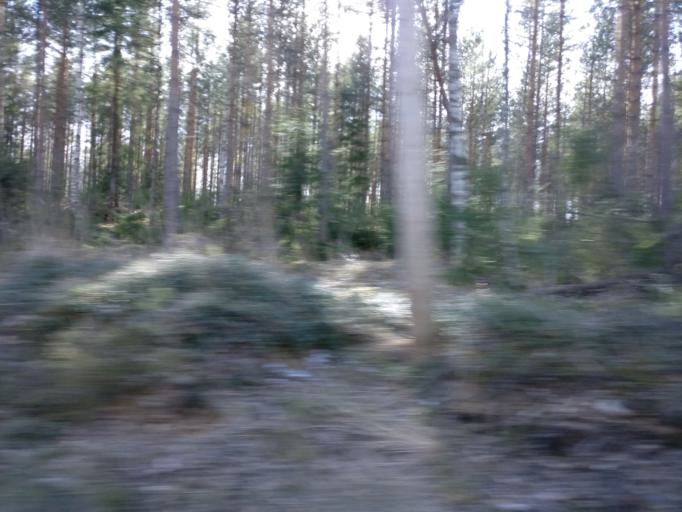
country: FI
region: Varsinais-Suomi
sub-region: Salo
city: Suomusjaervi
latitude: 60.3093
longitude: 23.6442
